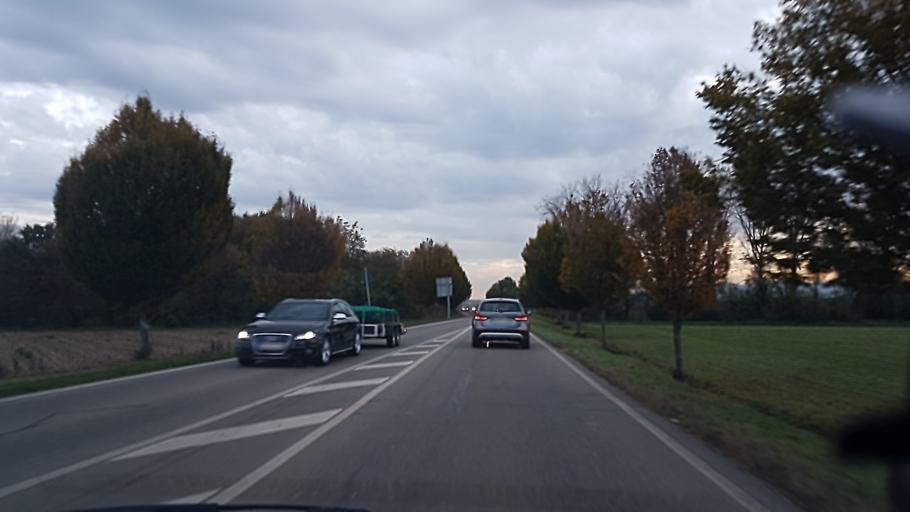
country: DE
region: Baden-Wuerttemberg
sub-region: Freiburg Region
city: Kenzingen
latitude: 48.1963
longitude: 7.7593
